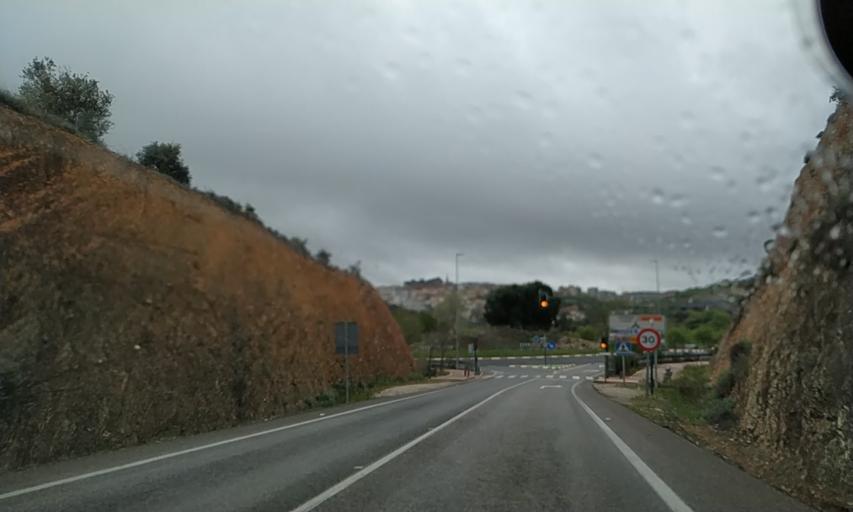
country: ES
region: Extremadura
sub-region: Provincia de Caceres
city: Caceres
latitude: 39.4871
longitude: -6.3828
